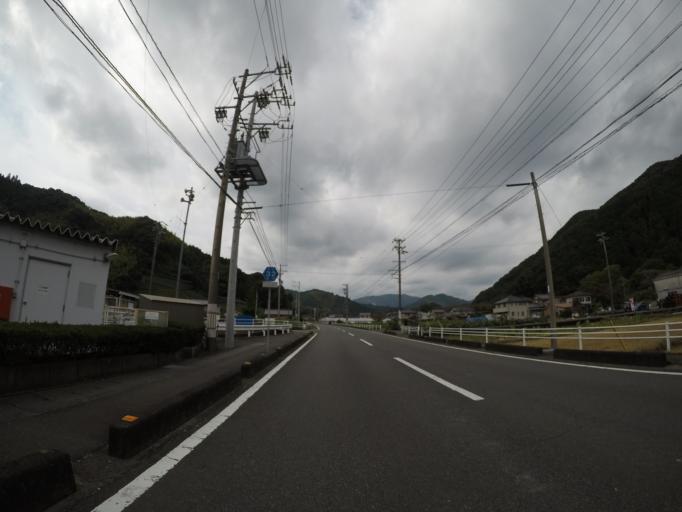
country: JP
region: Shizuoka
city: Fujieda
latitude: 34.8977
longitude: 138.2050
